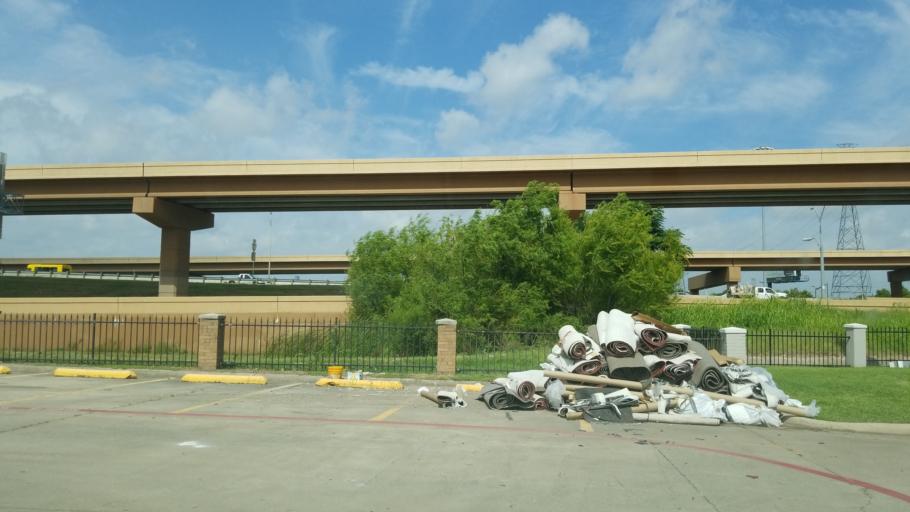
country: US
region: Texas
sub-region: Dallas County
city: Farmers Branch
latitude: 32.8825
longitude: -96.8970
